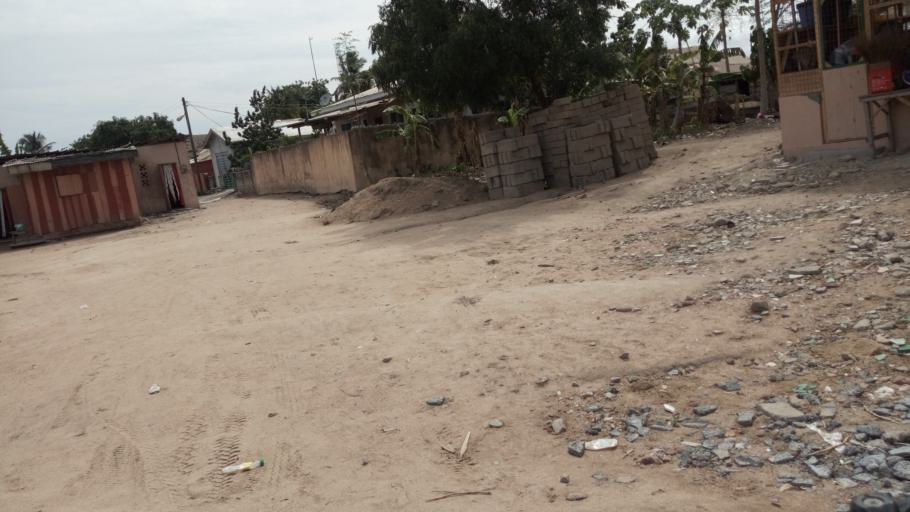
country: GH
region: Central
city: Winneba
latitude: 5.3494
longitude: -0.6255
